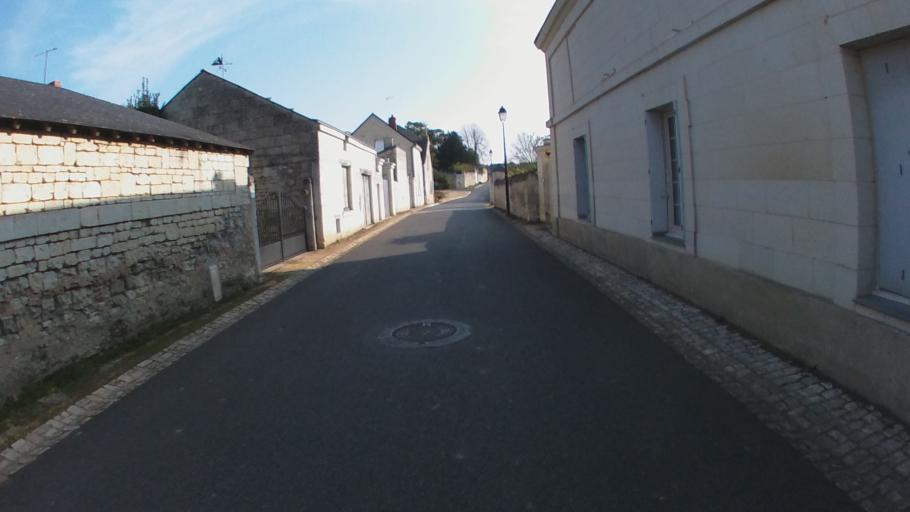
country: FR
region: Pays de la Loire
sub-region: Departement de Maine-et-Loire
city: Distre
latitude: 47.1943
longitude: -0.1228
